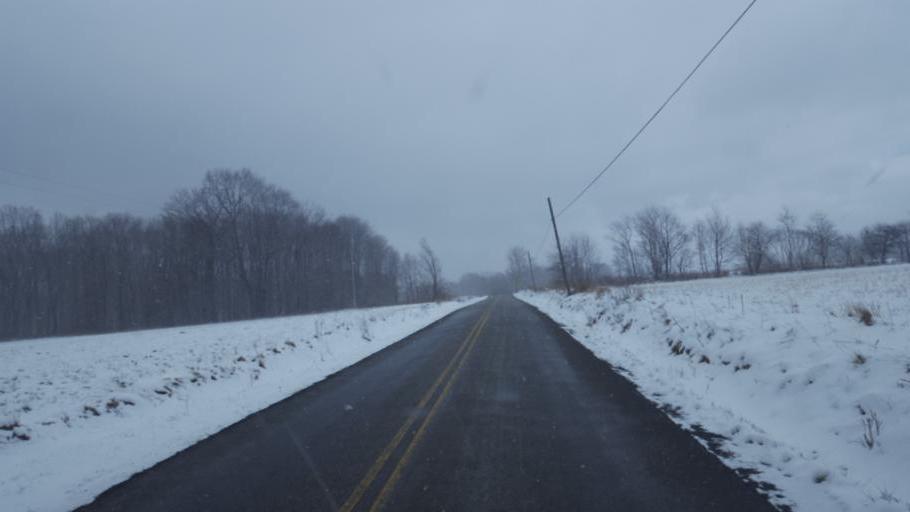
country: US
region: Pennsylvania
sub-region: Crawford County
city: Cochranton
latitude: 41.4267
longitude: -80.0222
